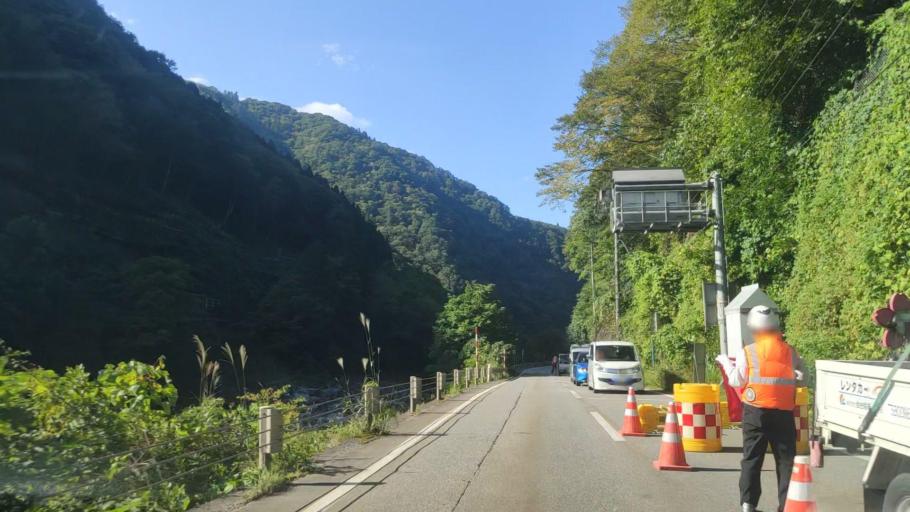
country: JP
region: Gifu
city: Takayama
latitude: 36.2828
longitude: 137.1305
